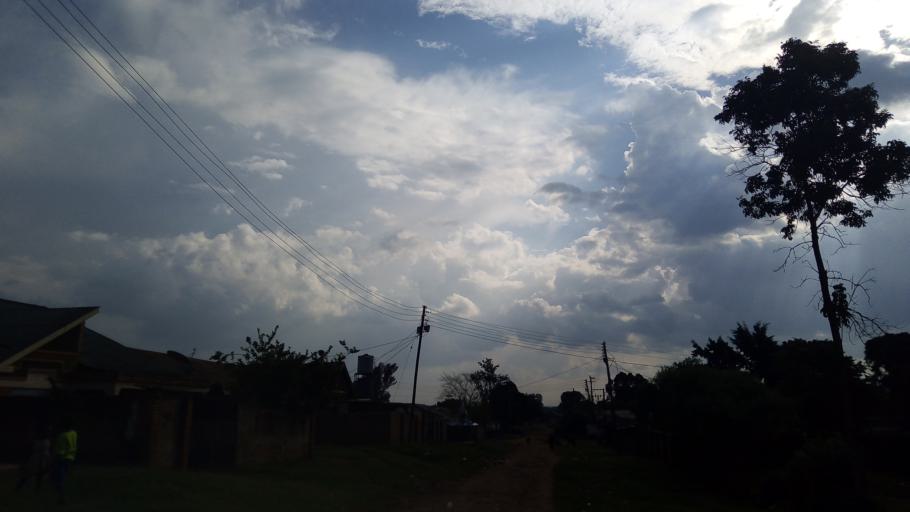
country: UG
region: Eastern Region
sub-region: Mbale District
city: Mbale
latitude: 1.0693
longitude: 34.1633
